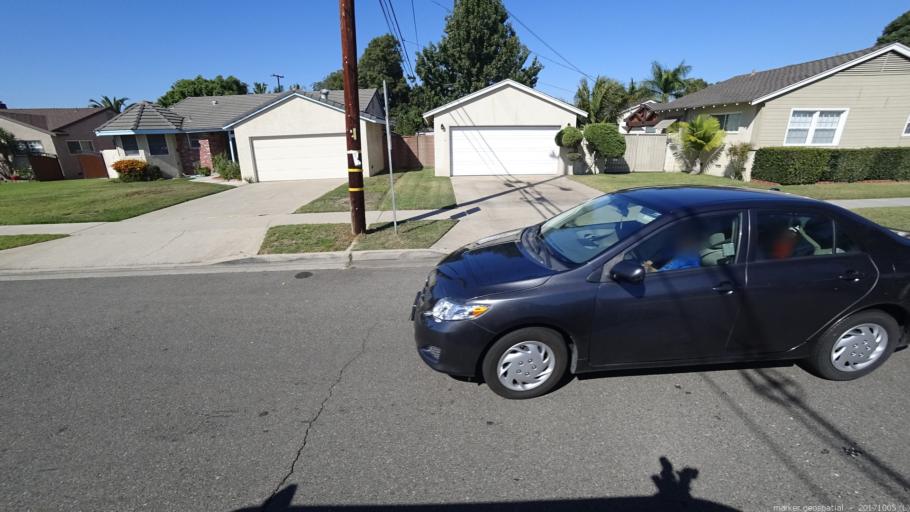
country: US
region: California
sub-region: Orange County
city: Garden Grove
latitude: 33.7855
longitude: -117.9460
